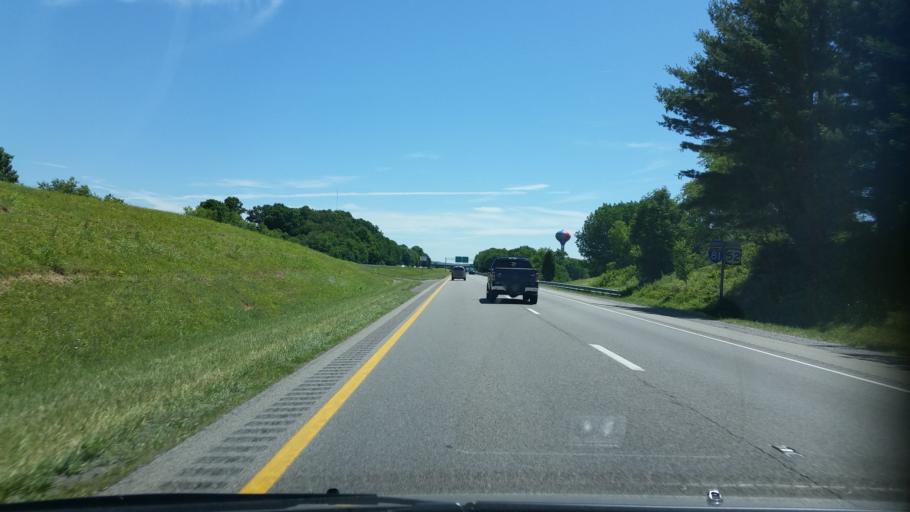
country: US
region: Virginia
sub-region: Wythe County
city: Wytheville
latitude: 36.9630
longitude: -81.0886
